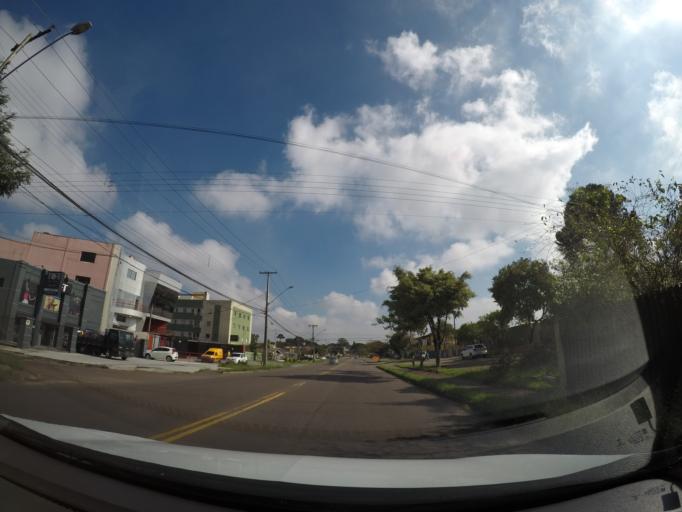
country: BR
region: Parana
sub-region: Sao Jose Dos Pinhais
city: Sao Jose dos Pinhais
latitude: -25.4934
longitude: -49.2198
